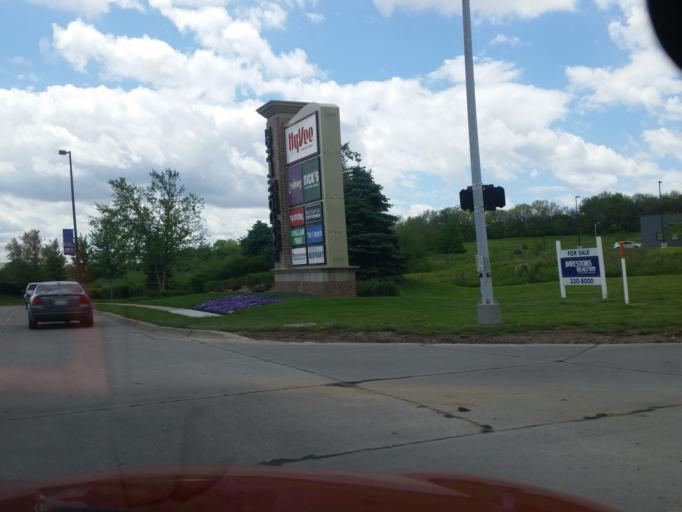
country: US
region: Nebraska
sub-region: Sarpy County
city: Papillion
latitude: 41.1390
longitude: -96.0301
